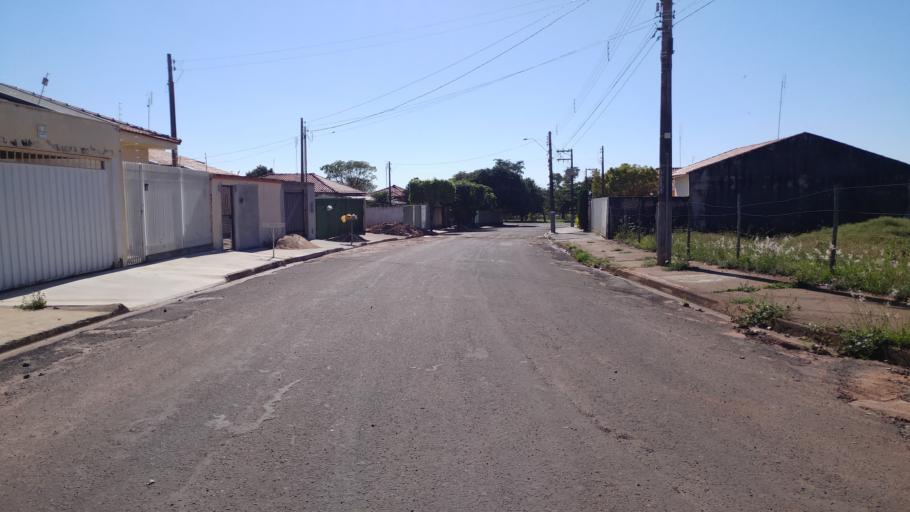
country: BR
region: Sao Paulo
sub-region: Paraguacu Paulista
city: Paraguacu Paulista
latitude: -22.4046
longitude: -50.5796
